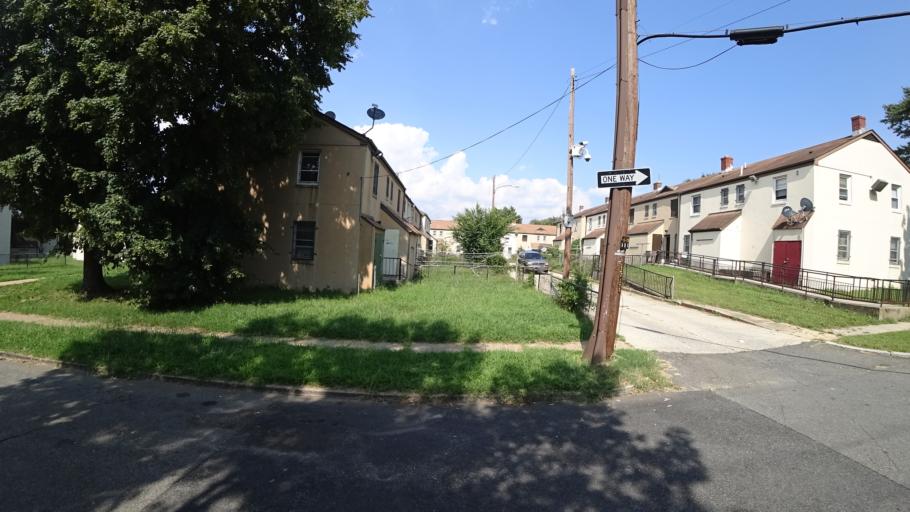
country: US
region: Maryland
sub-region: Prince George's County
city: Glassmanor
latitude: 38.8594
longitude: -76.9998
